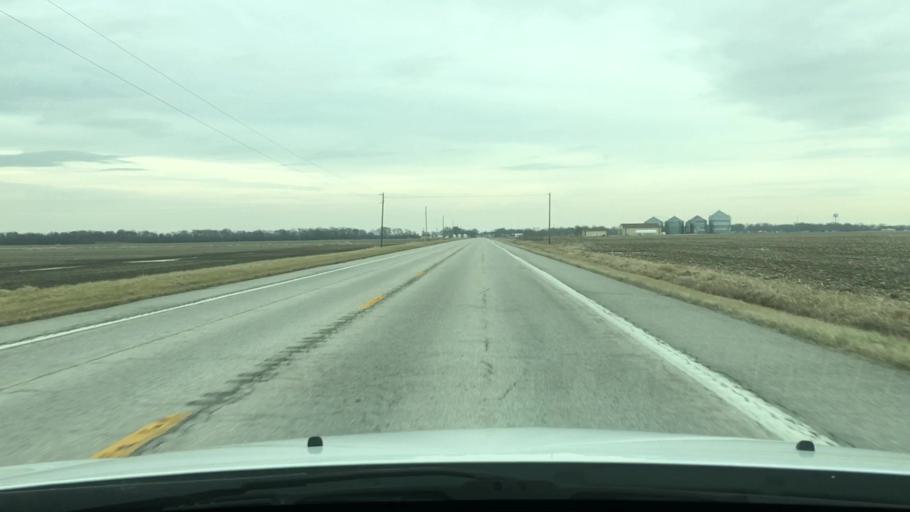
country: US
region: Missouri
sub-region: Audrain County
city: Vandalia
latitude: 39.2799
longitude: -91.6024
